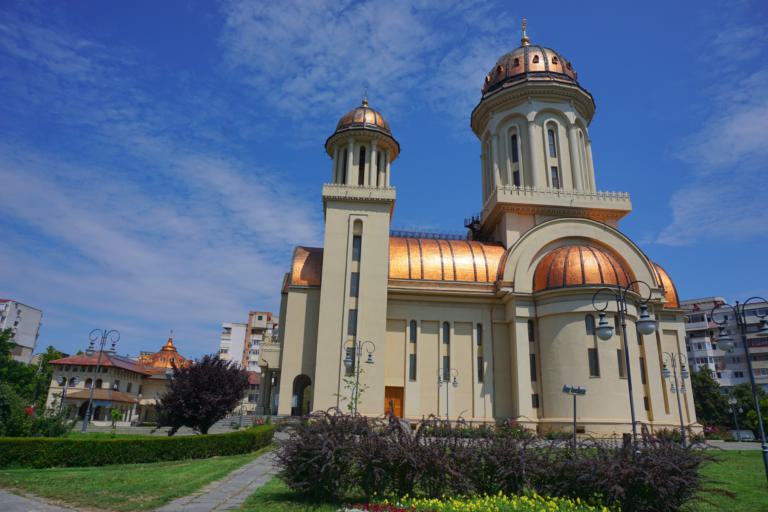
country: RO
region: Braila
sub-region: Municipiul Braila
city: Braila
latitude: 45.2579
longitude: 27.9599
